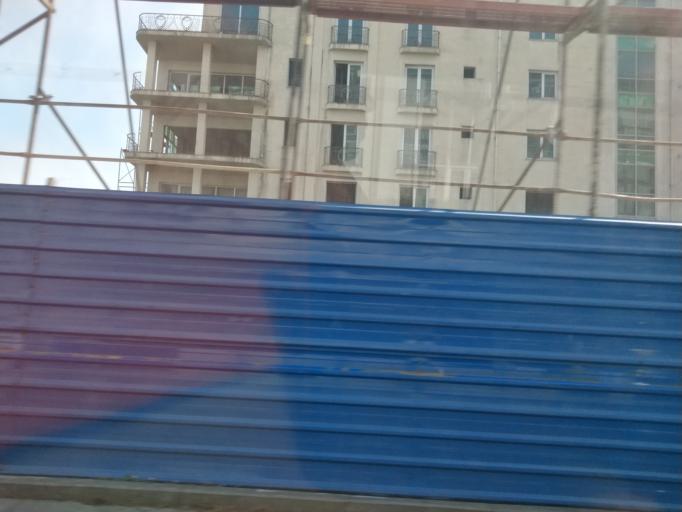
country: GE
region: Ajaria
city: Batumi
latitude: 41.6445
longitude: 41.6174
